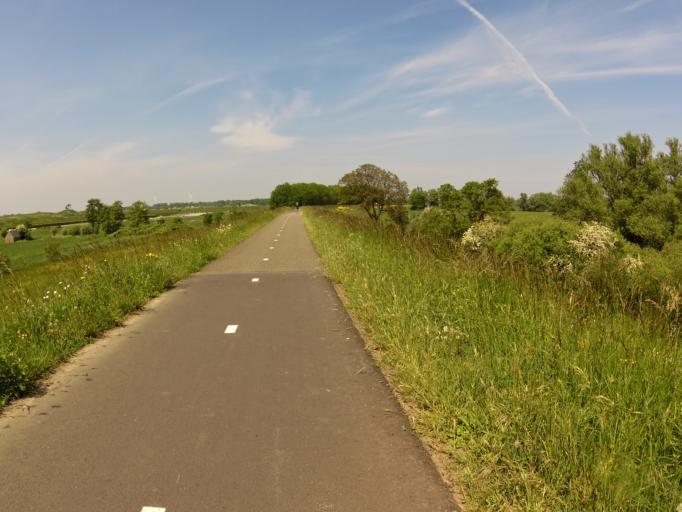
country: NL
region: Gelderland
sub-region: Gemeente Neerijnen
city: Neerijnen
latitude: 51.8130
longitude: 5.2826
